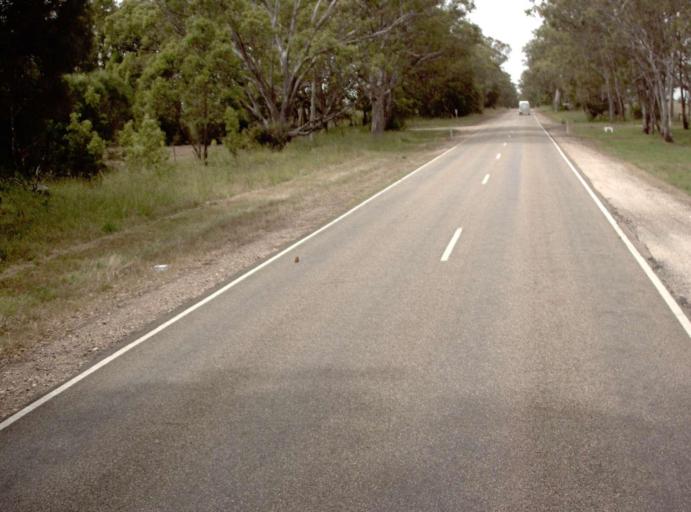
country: AU
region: Victoria
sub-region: Wellington
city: Sale
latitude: -37.9192
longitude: 147.0855
